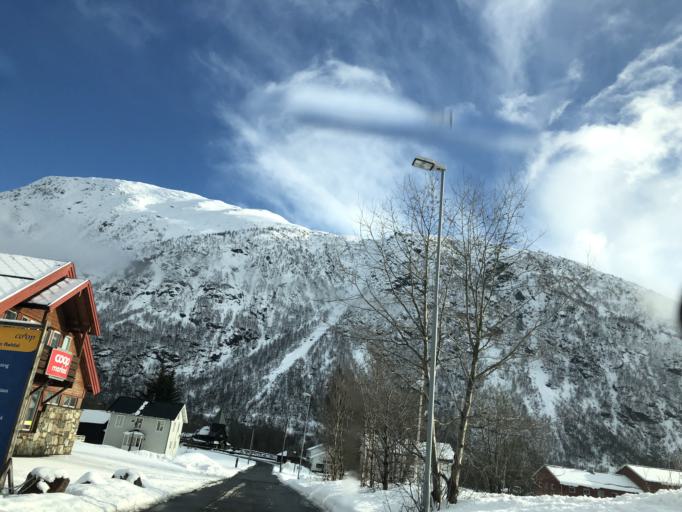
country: NO
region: Hordaland
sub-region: Odda
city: Odda
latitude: 59.8322
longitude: 6.8189
